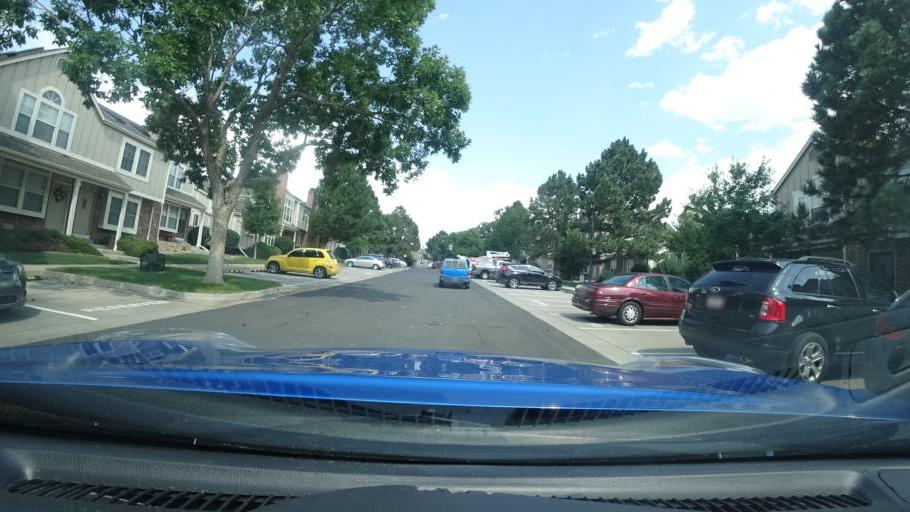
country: US
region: Colorado
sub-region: Adams County
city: Aurora
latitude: 39.6942
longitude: -104.7765
